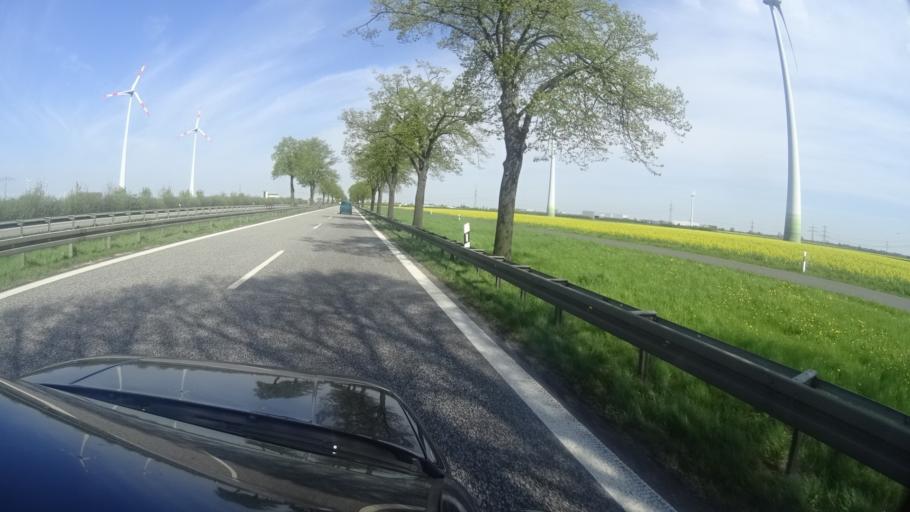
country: DE
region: Brandenburg
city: Nauen
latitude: 52.5860
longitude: 12.8983
